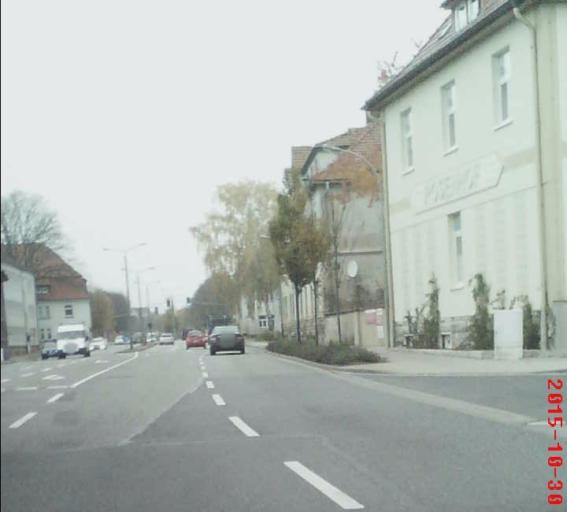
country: DE
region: Thuringia
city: Muehlhausen
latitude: 51.2161
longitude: 10.4627
